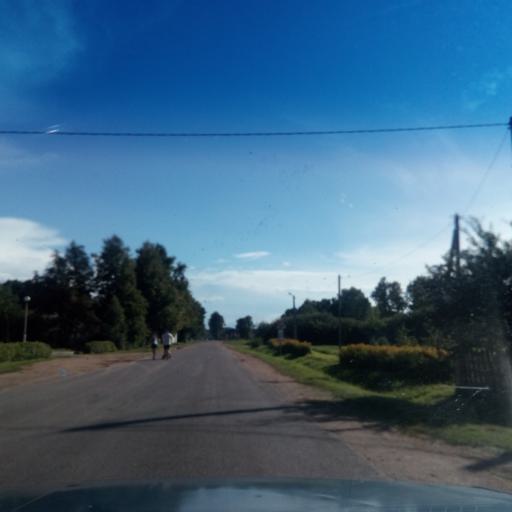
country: BY
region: Vitebsk
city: Dzisna
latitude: 55.6707
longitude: 28.3306
